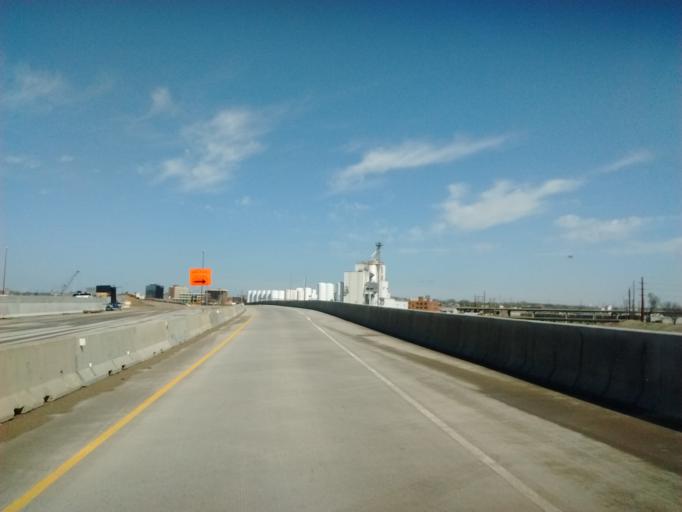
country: US
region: Iowa
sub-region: Woodbury County
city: Sioux City
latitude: 42.4838
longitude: -96.3910
